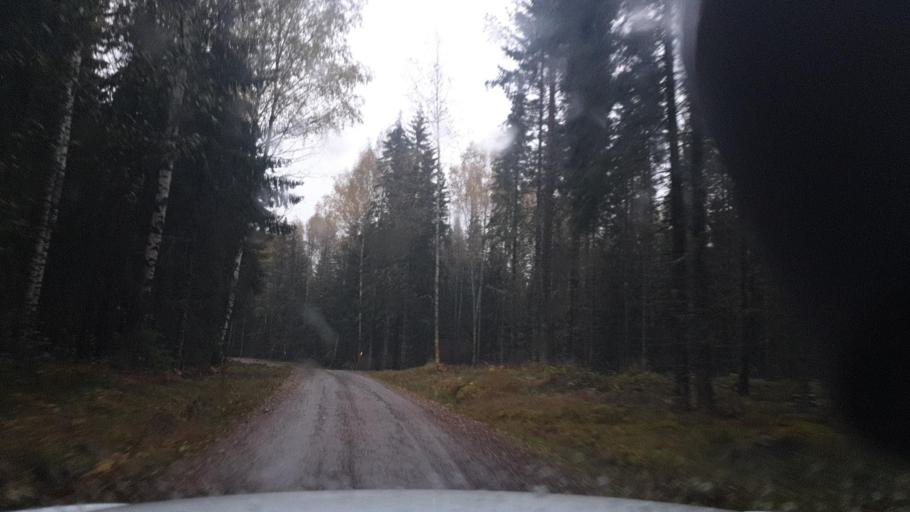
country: SE
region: Vaermland
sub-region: Eda Kommun
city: Amotfors
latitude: 59.8334
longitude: 12.3744
